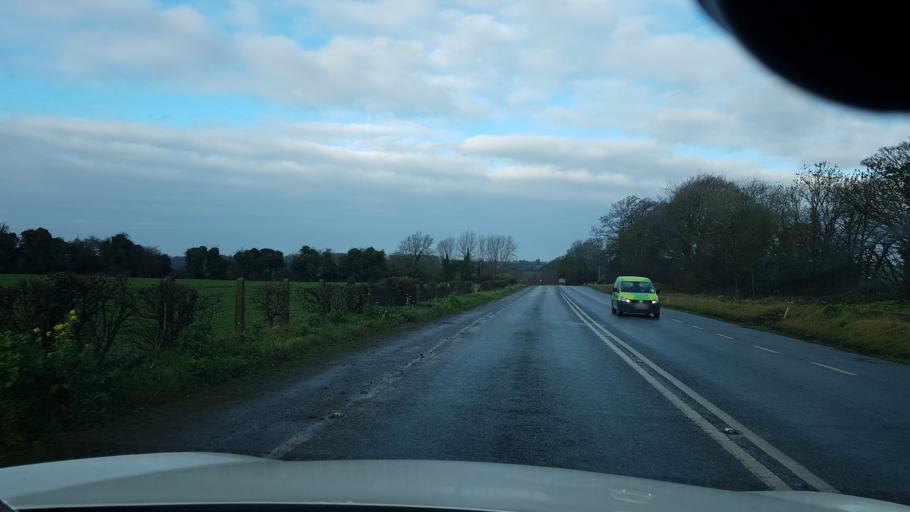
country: IE
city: Kentstown
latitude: 53.5948
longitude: -6.6071
